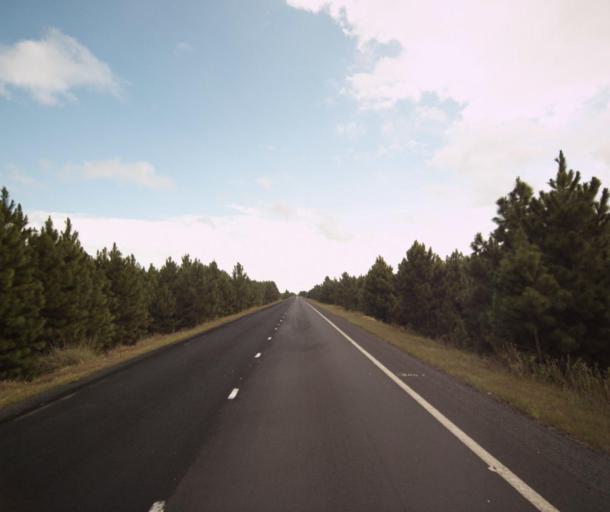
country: BR
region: Rio Grande do Sul
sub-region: Tapes
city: Tapes
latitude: -31.4209
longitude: -51.1791
